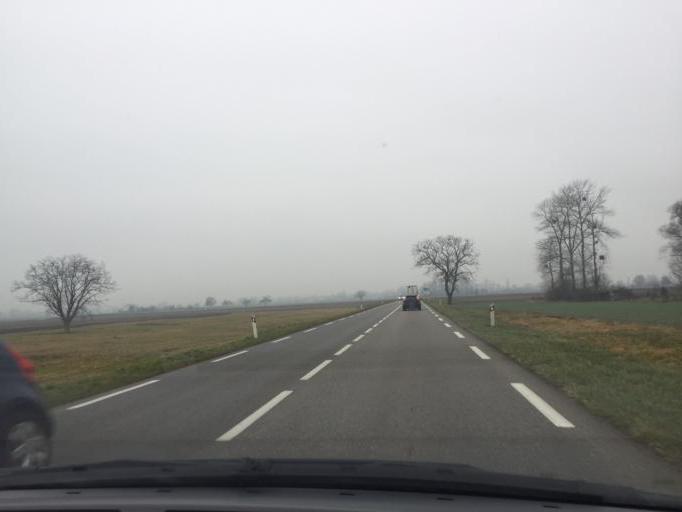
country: FR
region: Alsace
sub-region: Departement du Haut-Rhin
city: Andolsheim
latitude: 48.0562
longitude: 7.4399
